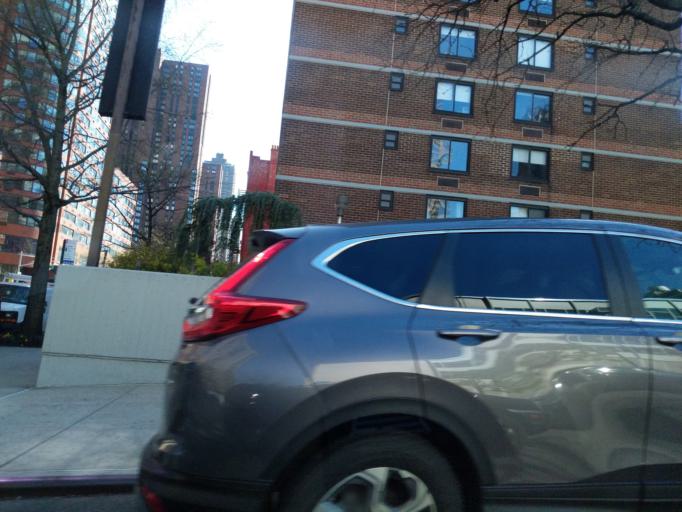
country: US
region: New York
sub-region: New York County
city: Manhattan
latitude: 40.7846
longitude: -73.9501
